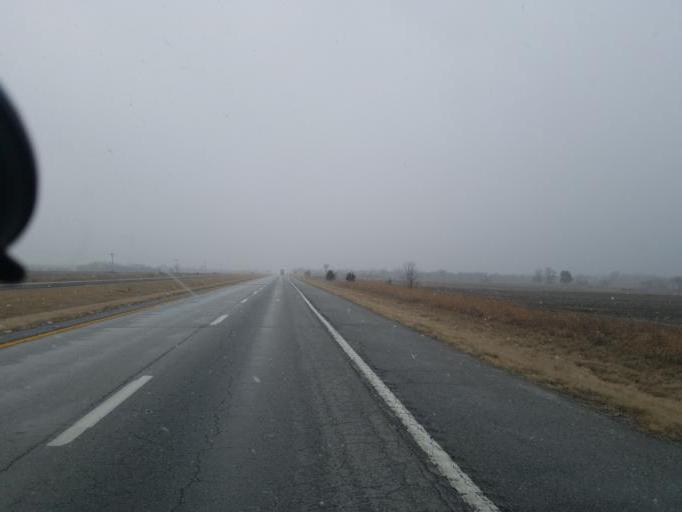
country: US
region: Missouri
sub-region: Macon County
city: La Plata
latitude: 39.9381
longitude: -92.4772
